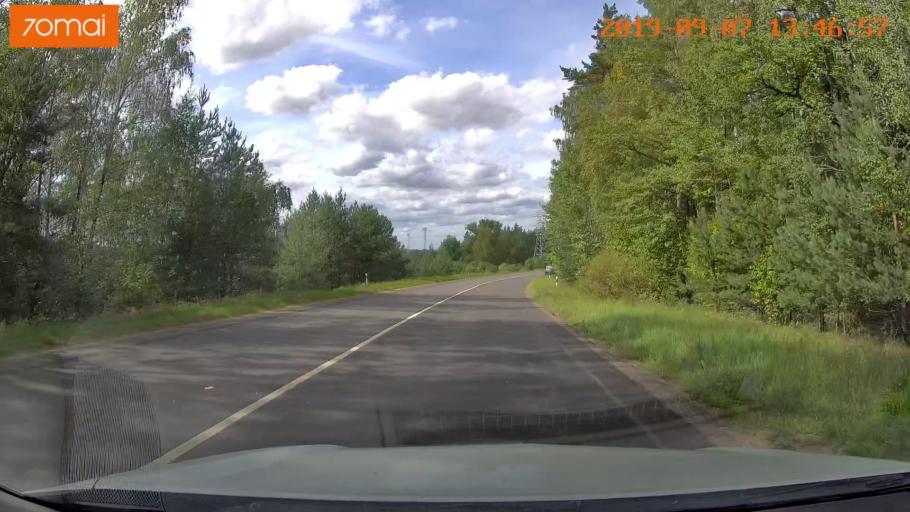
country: LT
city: Baltoji Voke
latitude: 54.5933
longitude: 25.2219
